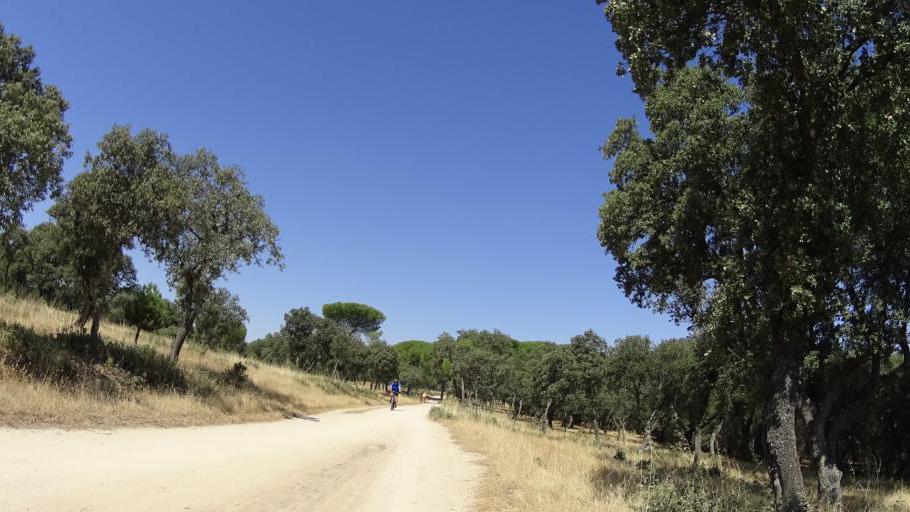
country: ES
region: Madrid
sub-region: Provincia de Madrid
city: Boadilla del Monte
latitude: 40.4362
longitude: -3.8596
